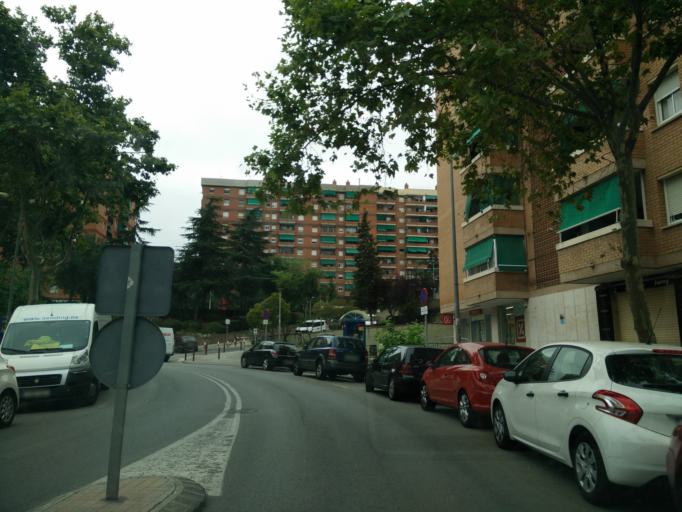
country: ES
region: Catalonia
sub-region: Provincia de Barcelona
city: Llefia
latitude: 41.4501
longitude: 2.2297
